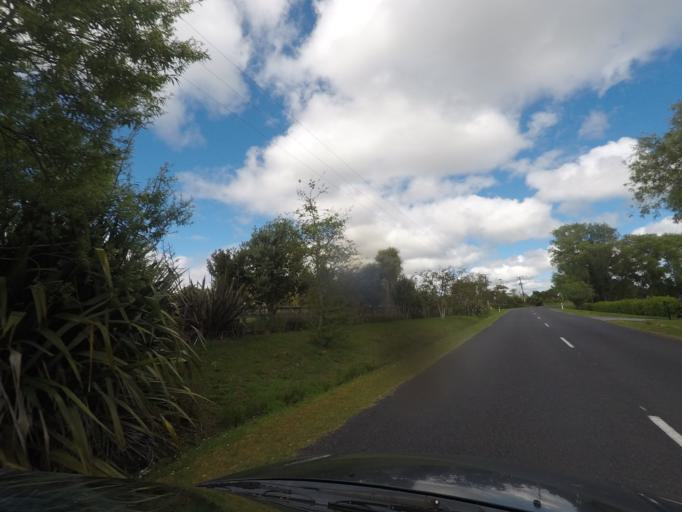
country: NZ
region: Auckland
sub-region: Auckland
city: Rothesay Bay
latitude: -36.7647
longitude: 174.6446
